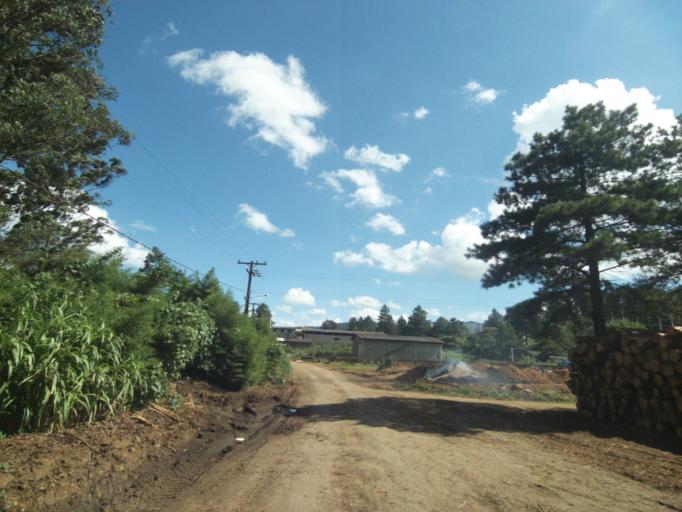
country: BR
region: Parana
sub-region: Uniao Da Vitoria
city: Uniao da Vitoria
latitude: -26.1508
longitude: -51.5387
